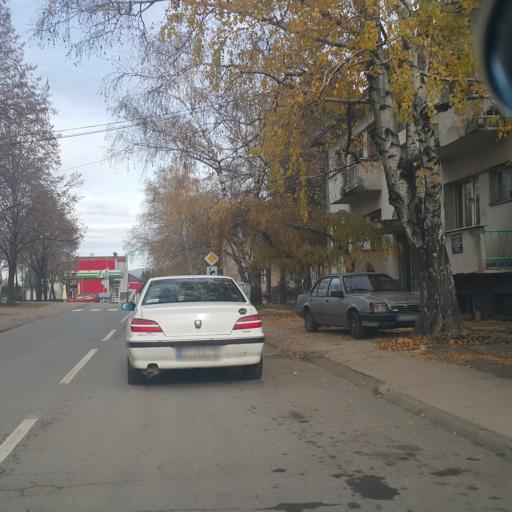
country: RS
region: Central Serbia
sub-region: Zajecarski Okrug
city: Knjazevac
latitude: 43.5707
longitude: 22.2516
